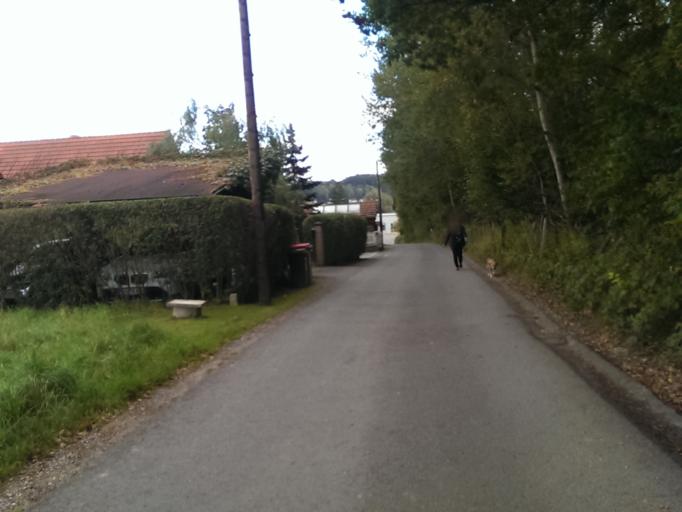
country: AT
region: Styria
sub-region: Politischer Bezirk Graz-Umgebung
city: Raaba
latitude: 47.0395
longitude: 15.4969
